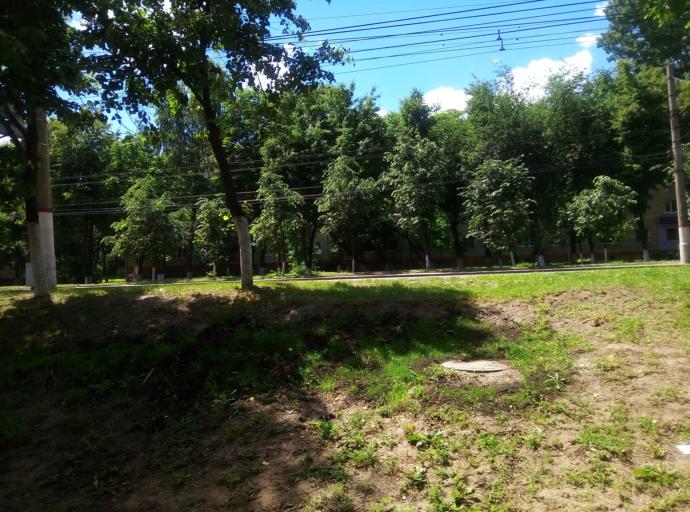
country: RU
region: Kursk
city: Kursk
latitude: 51.7687
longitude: 36.1822
